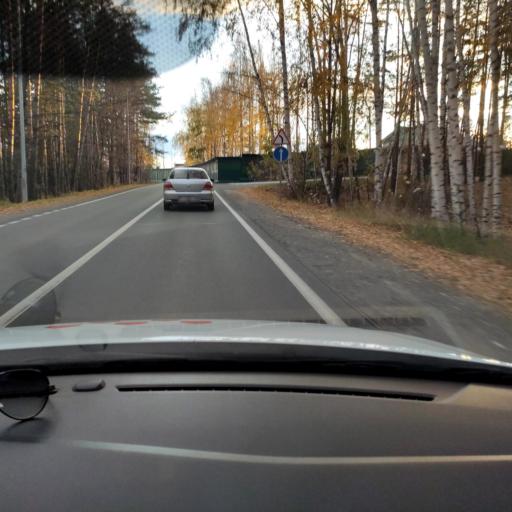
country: RU
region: Tatarstan
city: Verkhniy Uslon
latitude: 55.6302
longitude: 49.0157
